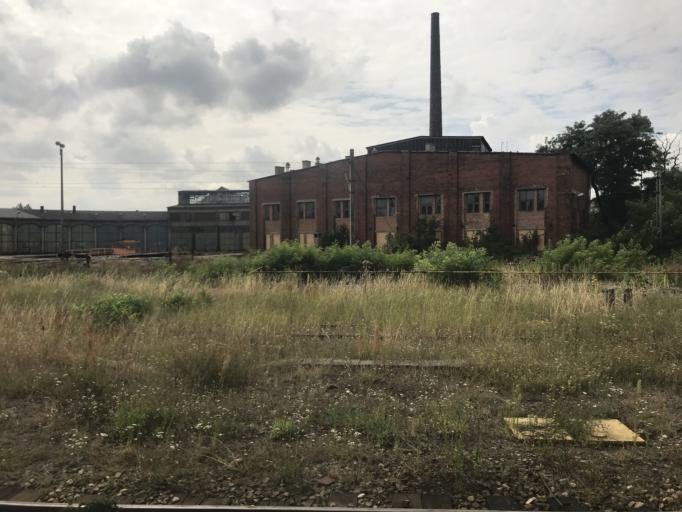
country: PL
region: Greater Poland Voivodeship
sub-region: Powiat gnieznienski
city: Gniezno
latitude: 52.5291
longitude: 17.5976
